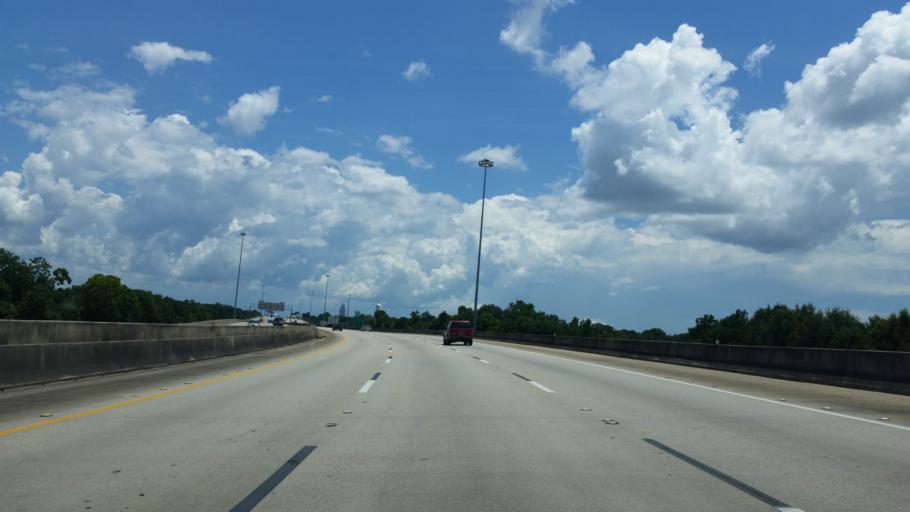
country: US
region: Alabama
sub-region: Mobile County
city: Prichard
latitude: 30.7411
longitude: -88.0887
